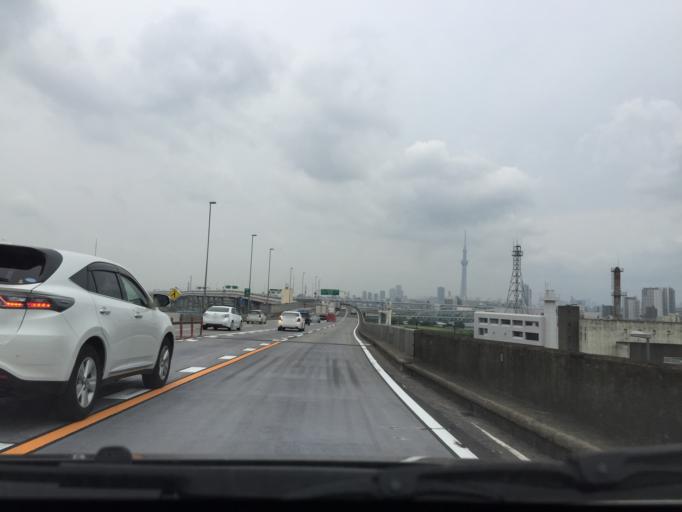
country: JP
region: Saitama
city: Soka
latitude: 35.7528
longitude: 139.8208
